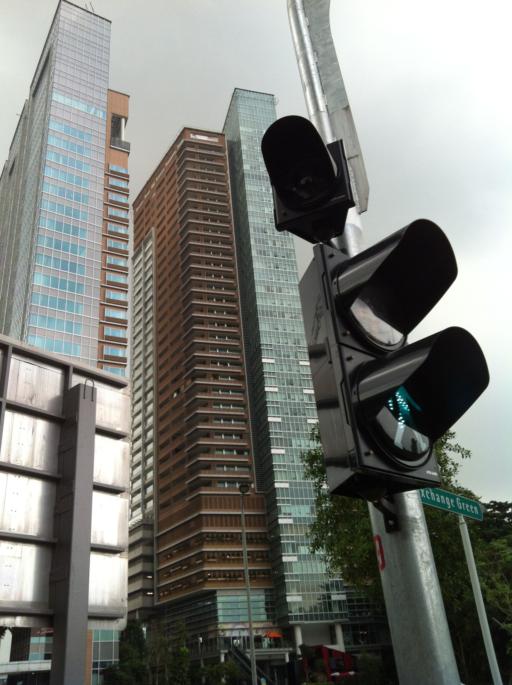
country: SG
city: Singapore
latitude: 1.3053
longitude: 103.7898
